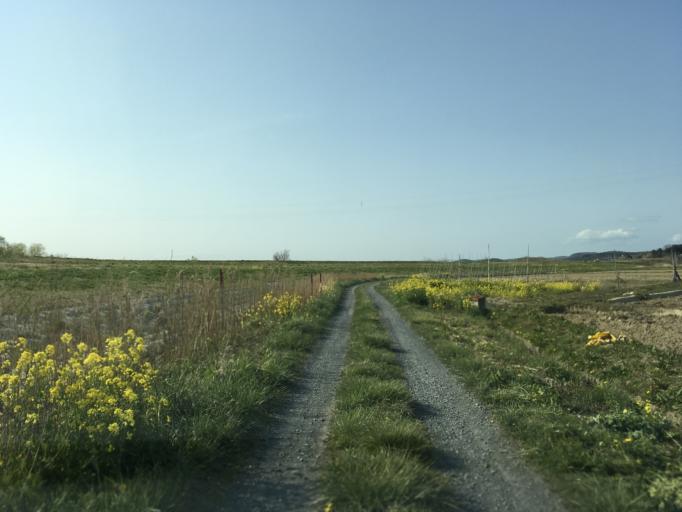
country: JP
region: Miyagi
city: Wakuya
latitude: 38.7135
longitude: 141.2699
